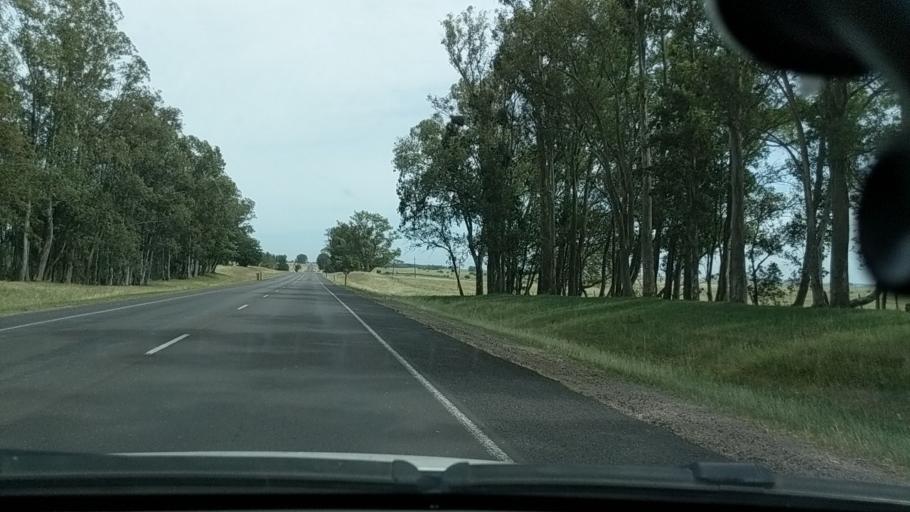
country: UY
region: Durazno
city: Durazno
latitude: -33.4734
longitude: -56.4516
